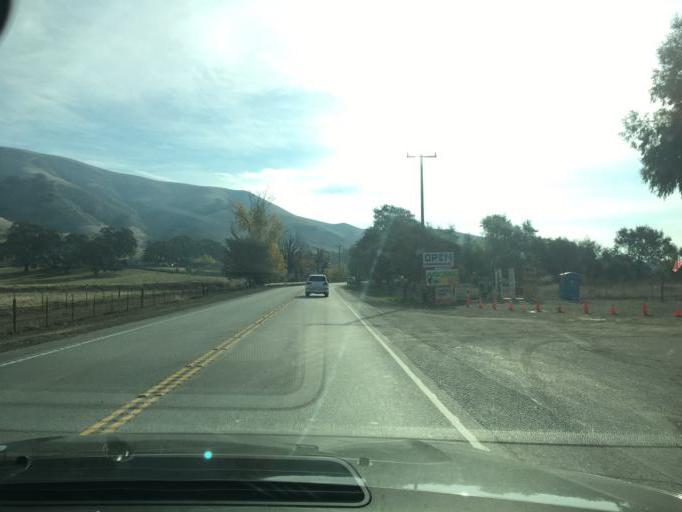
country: US
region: California
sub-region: Santa Clara County
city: Gilroy
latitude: 36.9854
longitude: -121.4427
